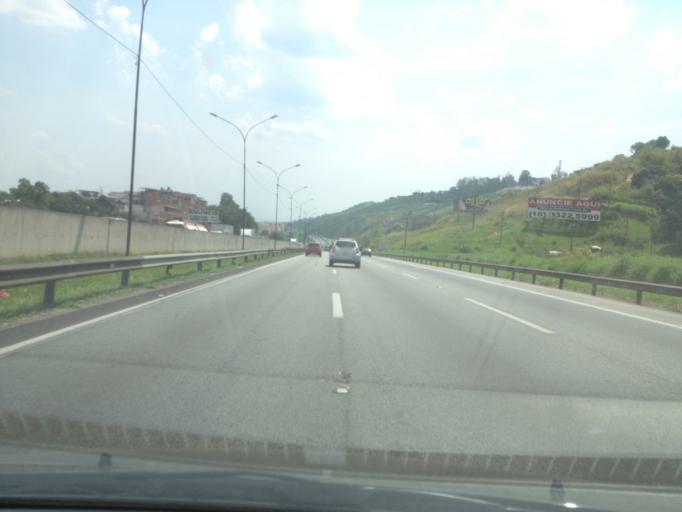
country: BR
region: Sao Paulo
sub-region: Barueri
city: Barueri
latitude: -23.5053
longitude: -46.8868
